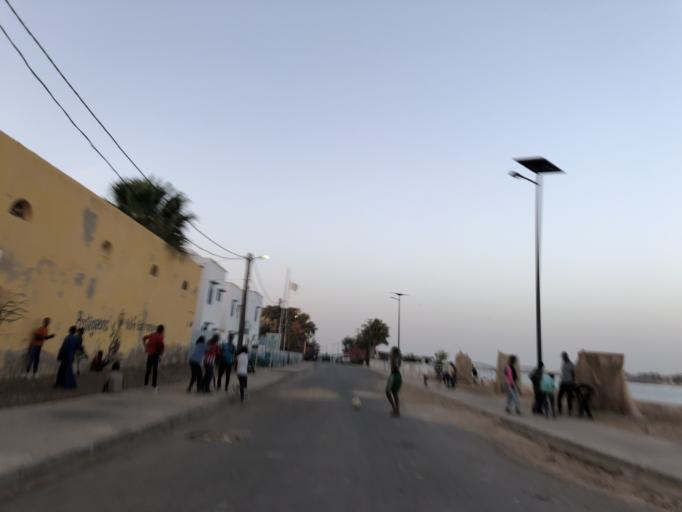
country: SN
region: Saint-Louis
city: Saint-Louis
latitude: 16.0197
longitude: -16.5047
